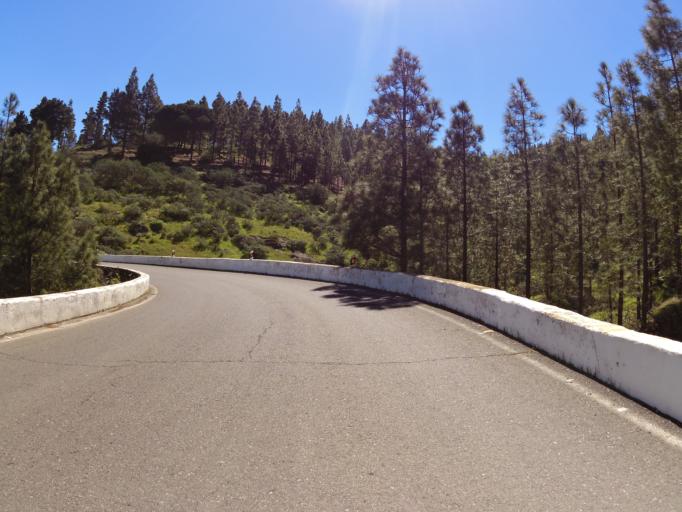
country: ES
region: Canary Islands
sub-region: Provincia de Las Palmas
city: Artenara
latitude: 28.0247
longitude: -15.6570
